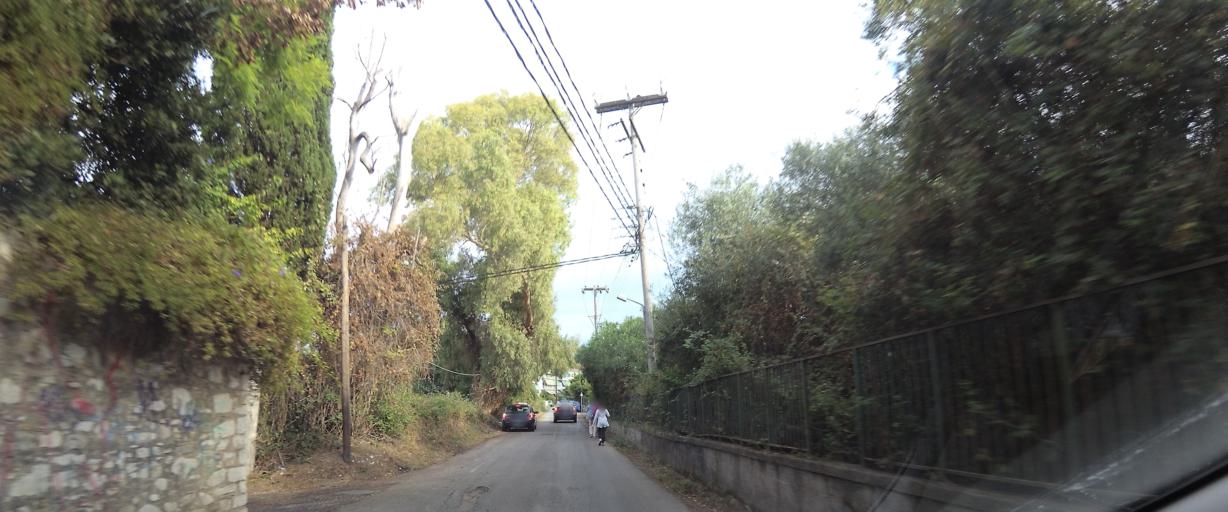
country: GR
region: Ionian Islands
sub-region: Nomos Kerkyras
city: Kerkyra
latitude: 39.6090
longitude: 19.9202
